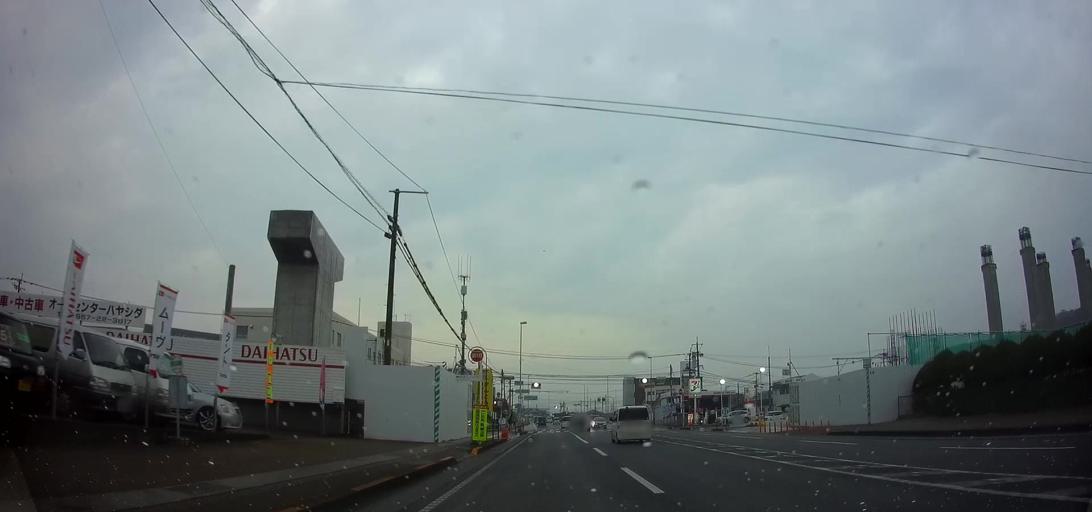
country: JP
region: Nagasaki
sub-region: Isahaya-shi
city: Isahaya
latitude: 32.8395
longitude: 130.0350
